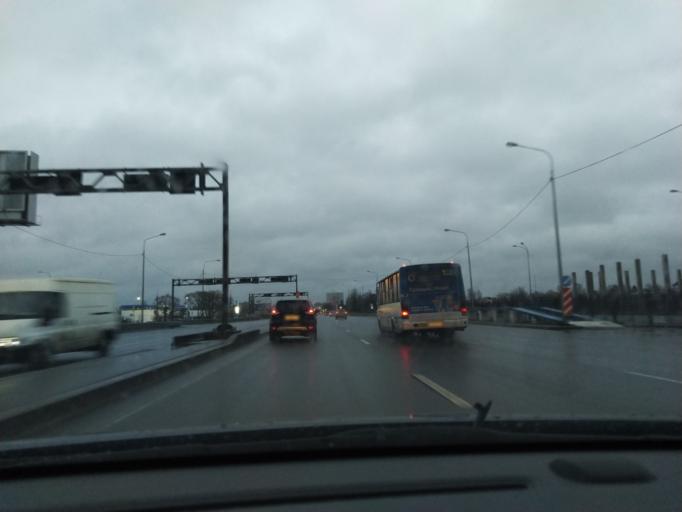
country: RU
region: St.-Petersburg
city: Uritsk
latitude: 59.8092
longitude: 30.1678
